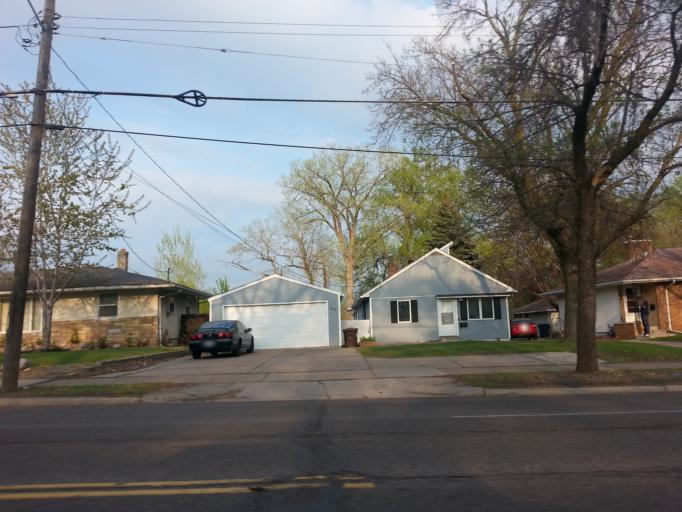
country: US
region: Minnesota
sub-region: Ramsey County
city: Maplewood
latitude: 44.9551
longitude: -93.0253
